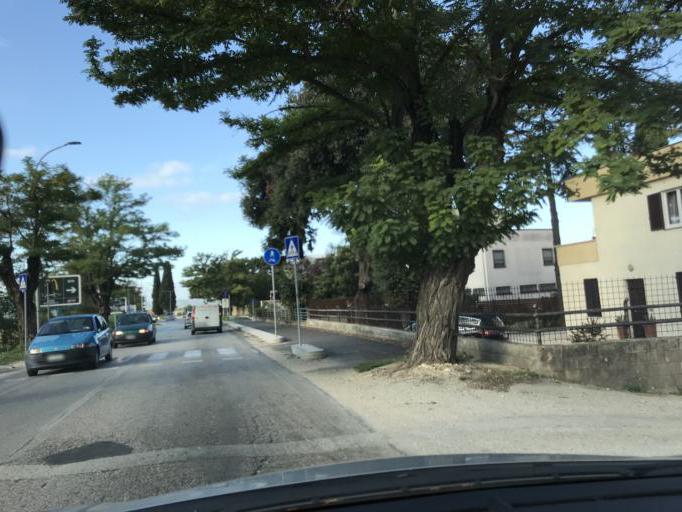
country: IT
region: Umbria
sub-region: Provincia di Perugia
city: Foligno
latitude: 42.9634
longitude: 12.6862
